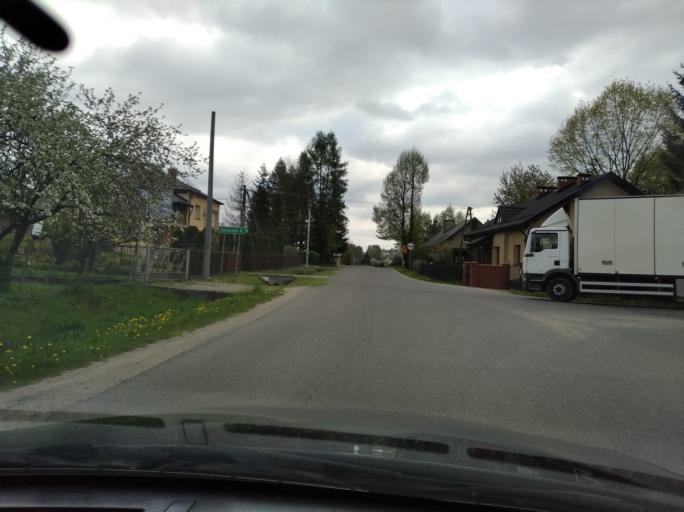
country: PL
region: Subcarpathian Voivodeship
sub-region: Powiat debicki
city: Leki Gorne
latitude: 49.9745
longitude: 21.2073
